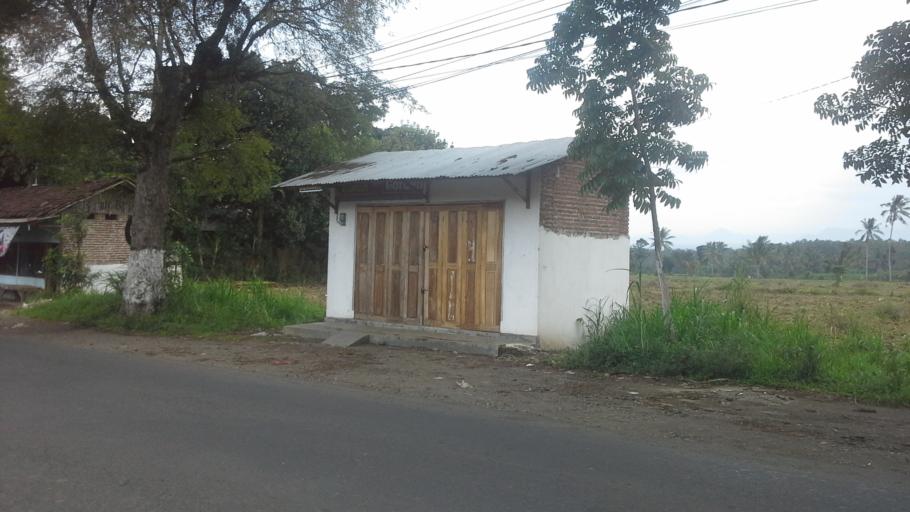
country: ID
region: East Java
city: Krajan Satu Pekauman
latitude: -7.9783
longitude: 113.7961
